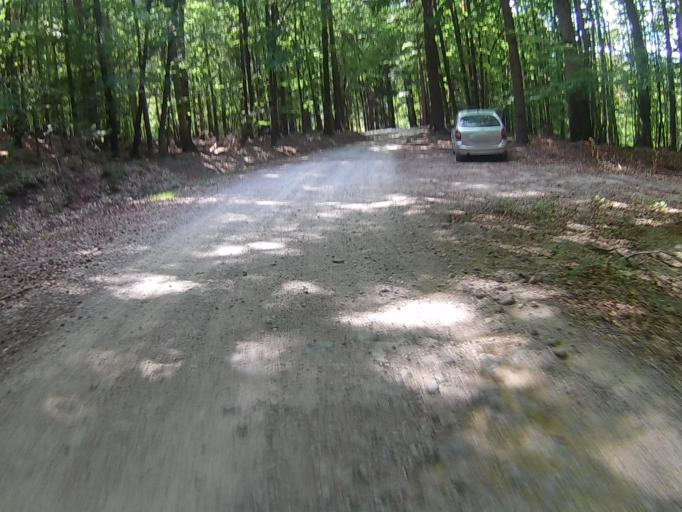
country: SI
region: Maribor
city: Pekre
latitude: 46.5247
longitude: 15.5786
